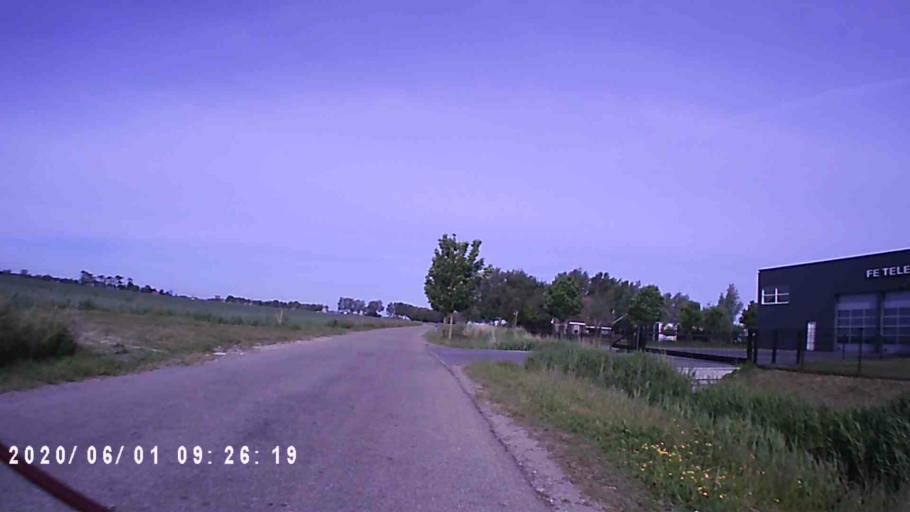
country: NL
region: Friesland
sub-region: Gemeente Leeuwarderadeel
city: Stiens
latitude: 53.2655
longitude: 5.7466
